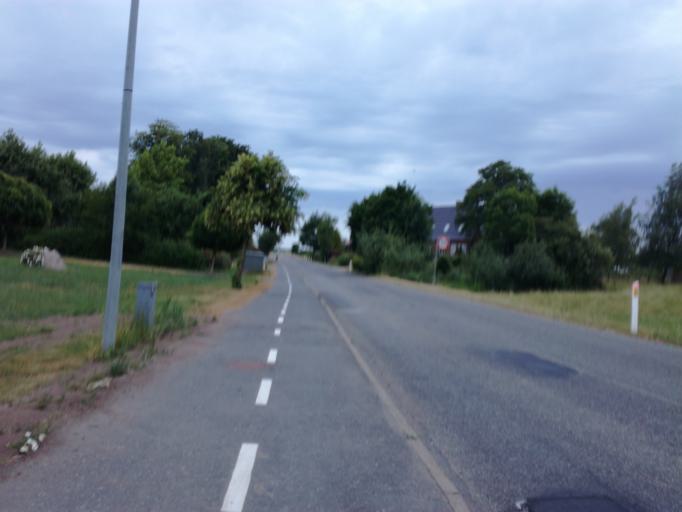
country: DK
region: South Denmark
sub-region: Vejle Kommune
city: Borkop
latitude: 55.6671
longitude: 9.6245
